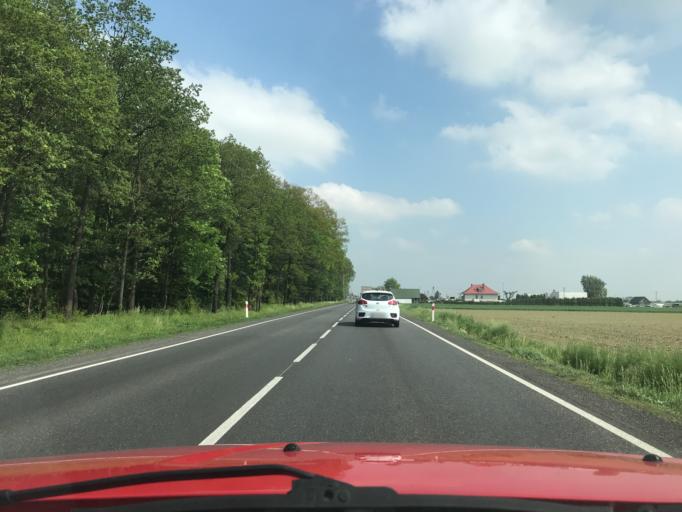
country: PL
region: Greater Poland Voivodeship
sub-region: Powiat pleszewski
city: Czermin
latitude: 51.9069
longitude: 17.7313
